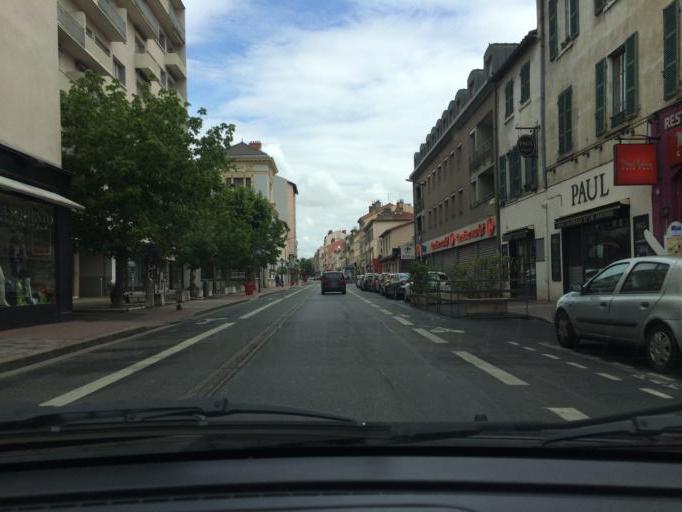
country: FR
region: Rhone-Alpes
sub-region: Departement du Rhone
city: Lyon
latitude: 45.7454
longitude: 4.8652
